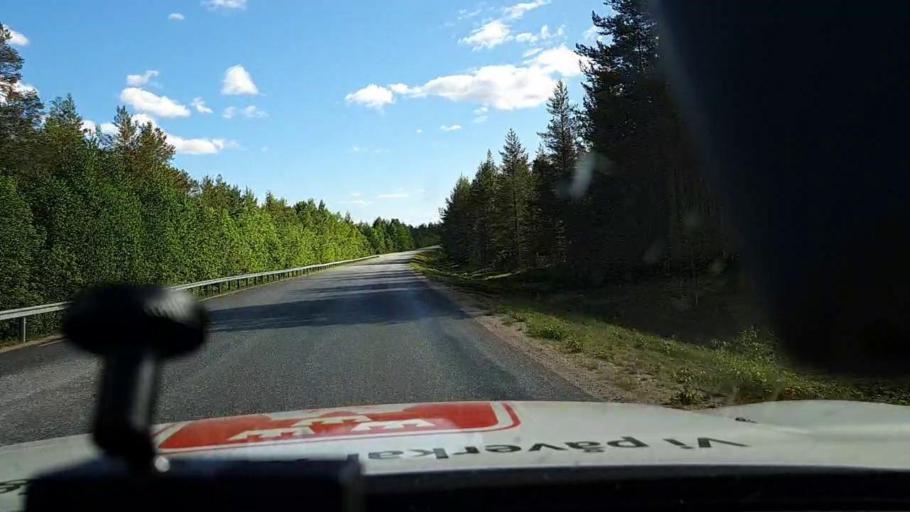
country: SE
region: Norrbotten
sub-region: Overtornea Kommun
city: OEvertornea
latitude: 66.3450
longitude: 23.6483
